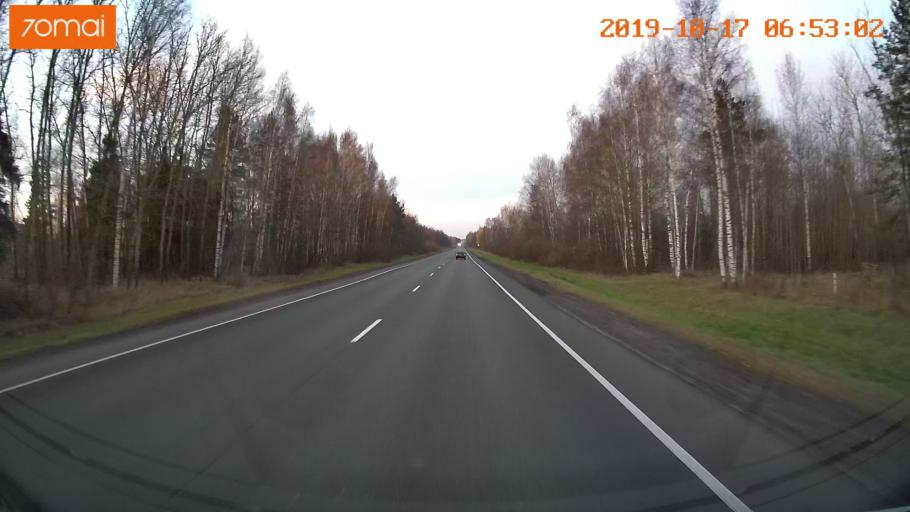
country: RU
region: Vladimir
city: Kideksha
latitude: 56.4794
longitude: 40.4946
